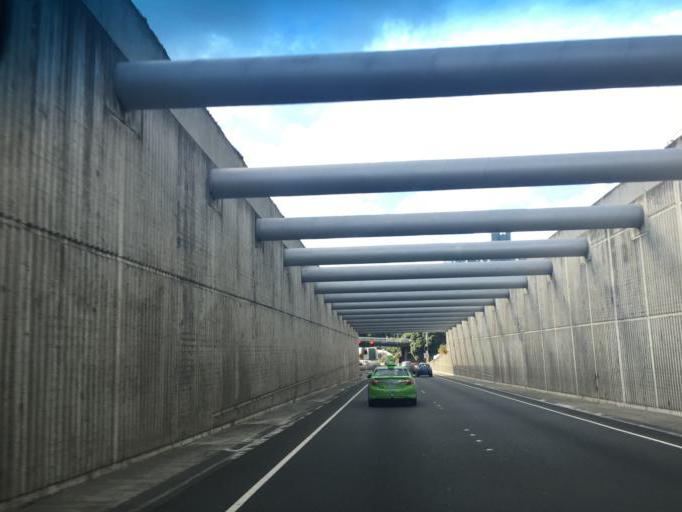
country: NZ
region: Wellington
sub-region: Wellington City
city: Wellington
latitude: -41.2937
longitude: 174.7711
